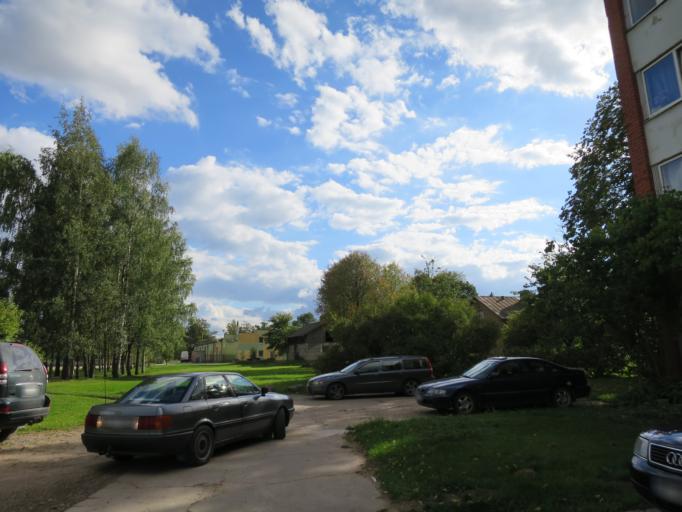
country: LV
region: Sigulda
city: Sigulda
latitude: 57.1493
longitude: 24.8959
